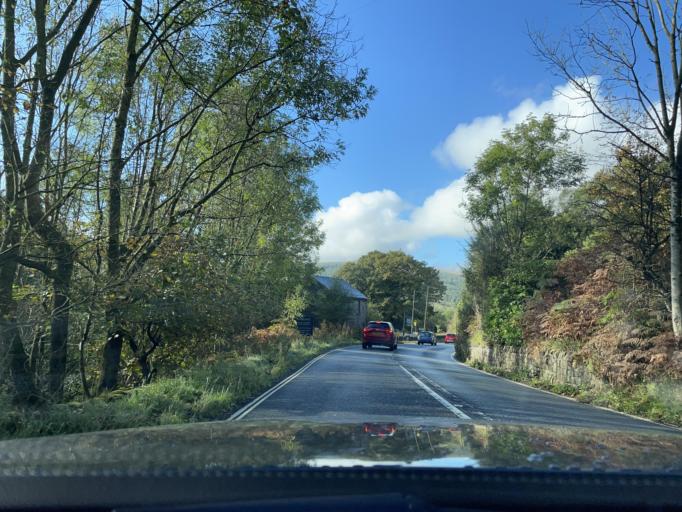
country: GB
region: England
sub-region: Derbyshire
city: Hope Valley
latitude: 53.3753
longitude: -1.6929
